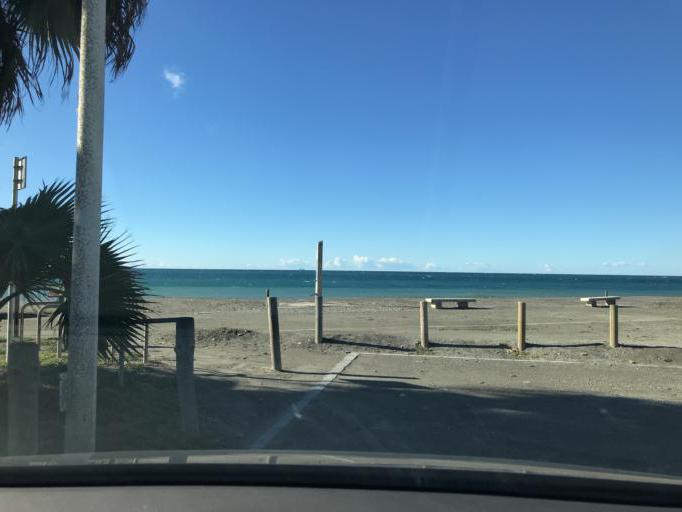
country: ES
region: Andalusia
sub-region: Provincia de Granada
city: Salobrena
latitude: 36.7183
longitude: -3.5621
